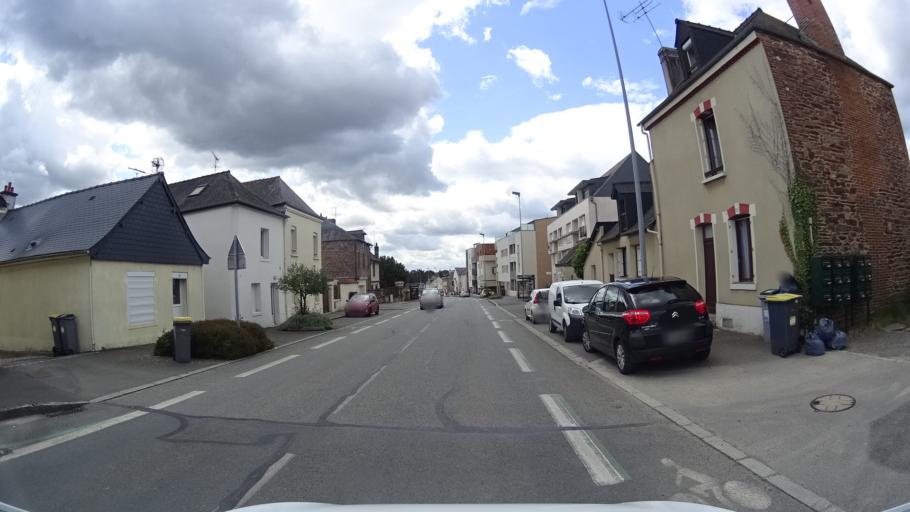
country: FR
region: Brittany
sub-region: Departement d'Ille-et-Vilaine
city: Chartres-de-Bretagne
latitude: 48.0341
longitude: -1.7121
